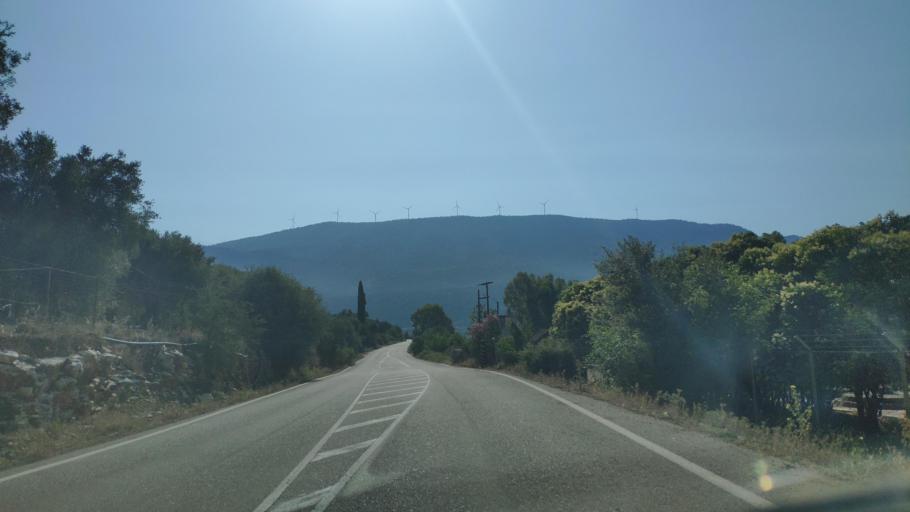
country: GR
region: West Greece
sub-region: Nomos Aitolias kai Akarnanias
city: Stanos
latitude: 38.7694
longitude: 21.1761
